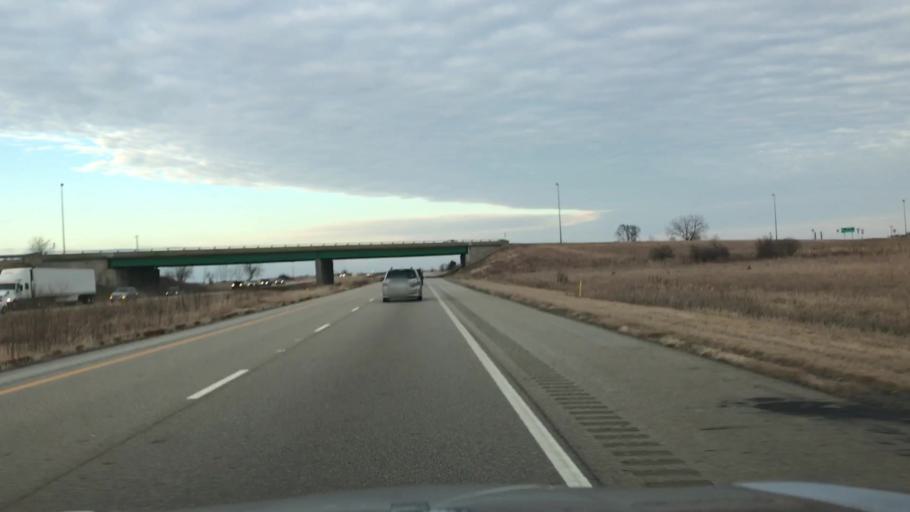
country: US
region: Illinois
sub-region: Logan County
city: Atlanta
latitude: 40.2584
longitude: -89.2211
